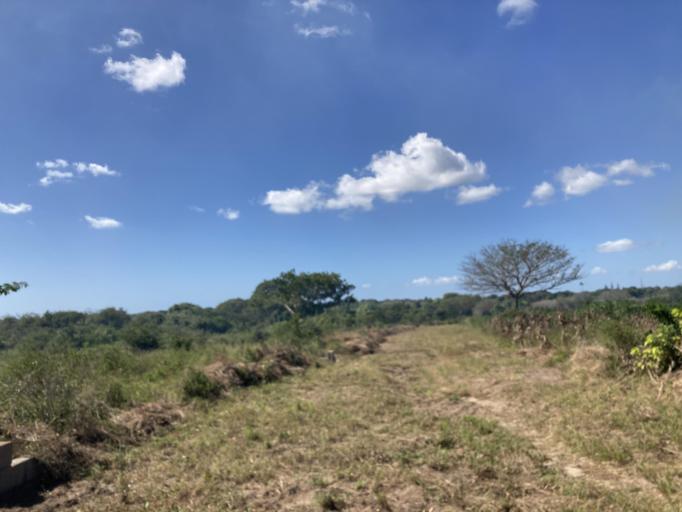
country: MZ
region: Maputo City
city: Maputo
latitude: -26.0506
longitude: 32.5517
